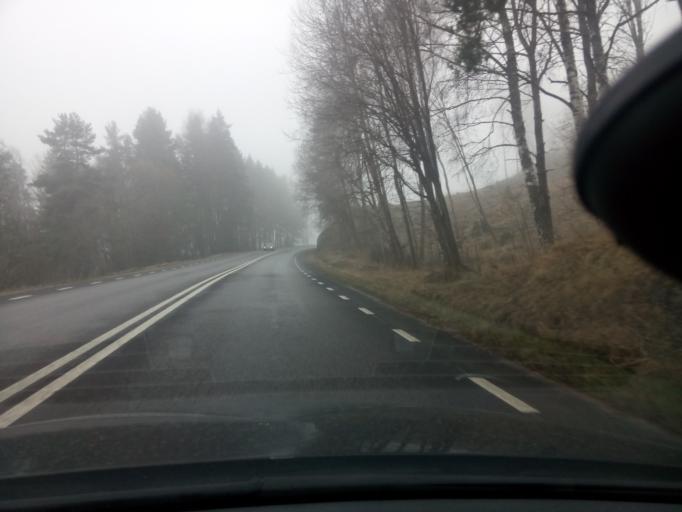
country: SE
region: Soedermanland
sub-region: Nykopings Kommun
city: Nykoping
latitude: 58.8003
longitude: 17.0834
